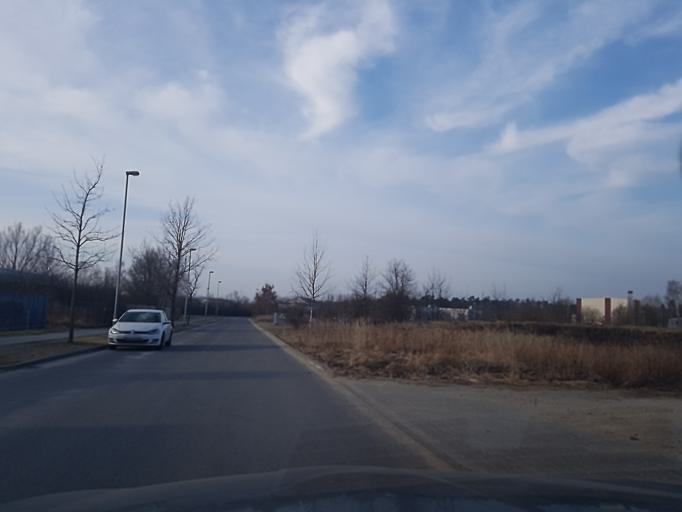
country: DE
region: Brandenburg
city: Finsterwalde
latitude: 51.6334
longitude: 13.7431
